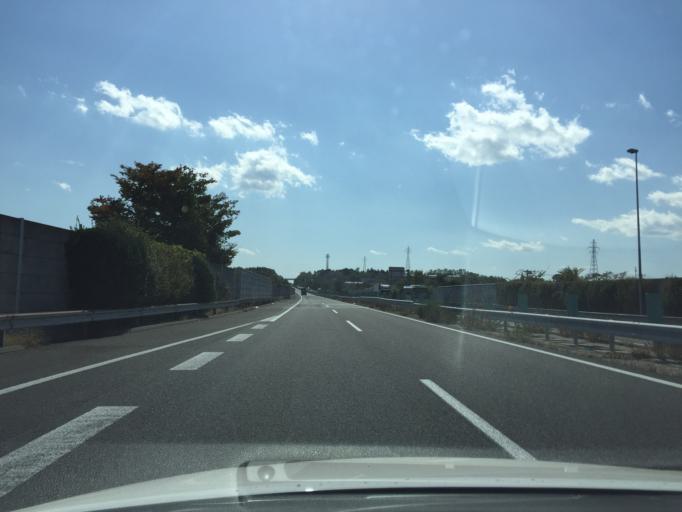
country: JP
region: Fukushima
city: Sukagawa
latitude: 37.2876
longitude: 140.3510
